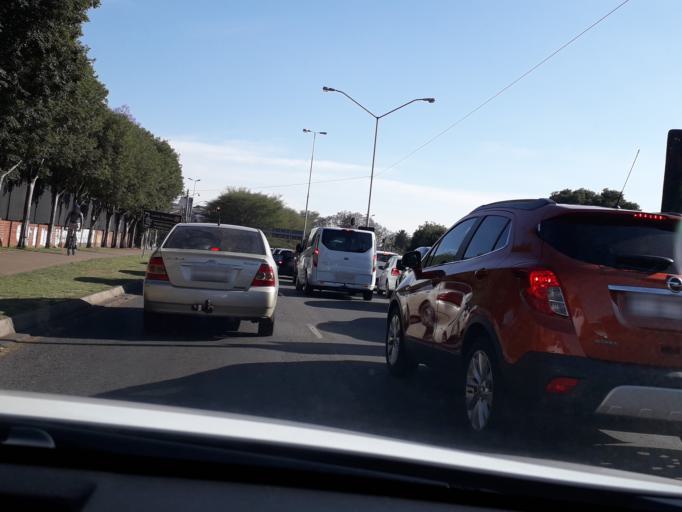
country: ZA
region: Gauteng
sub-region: City of Tshwane Metropolitan Municipality
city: Pretoria
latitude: -25.7526
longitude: 28.1978
